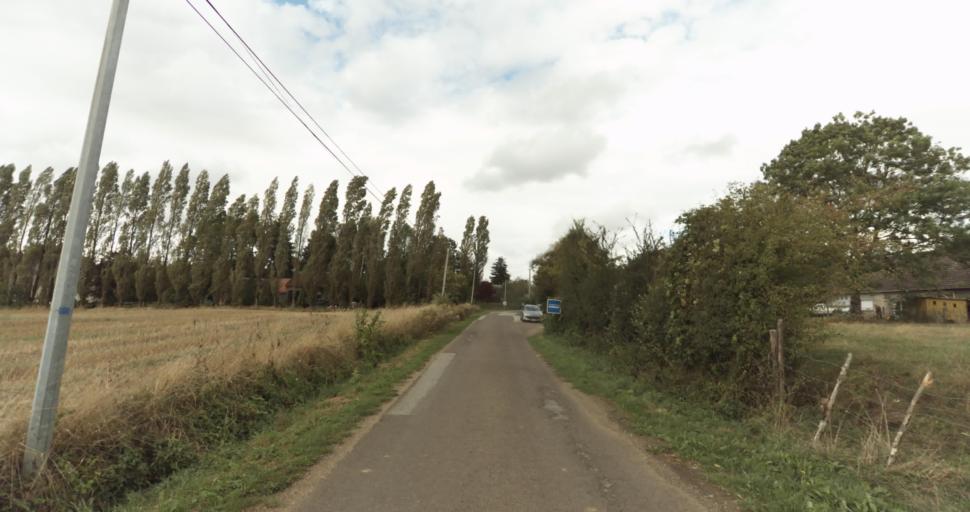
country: FR
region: Lower Normandy
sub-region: Departement de l'Orne
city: Sainte-Gauburge-Sainte-Colombe
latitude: 48.7487
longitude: 0.3791
